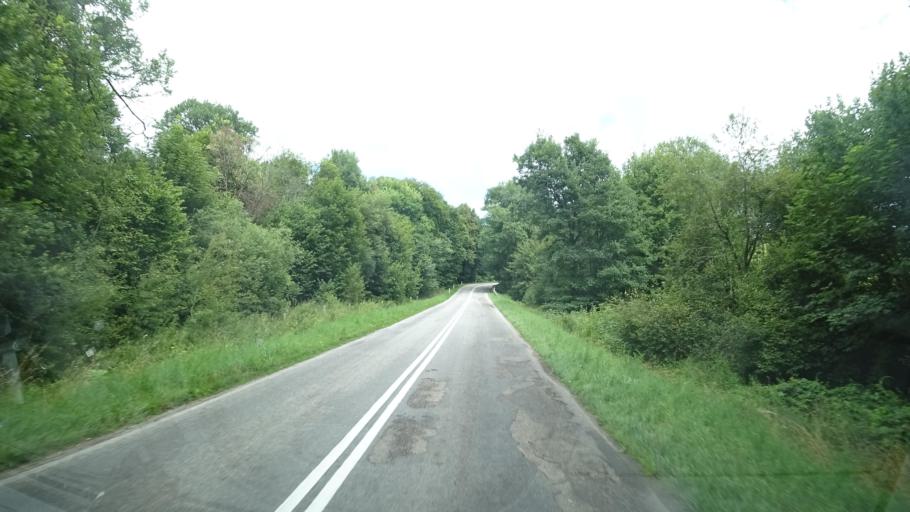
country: PL
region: Warmian-Masurian Voivodeship
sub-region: Powiat goldapski
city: Goldap
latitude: 54.2099
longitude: 22.2035
